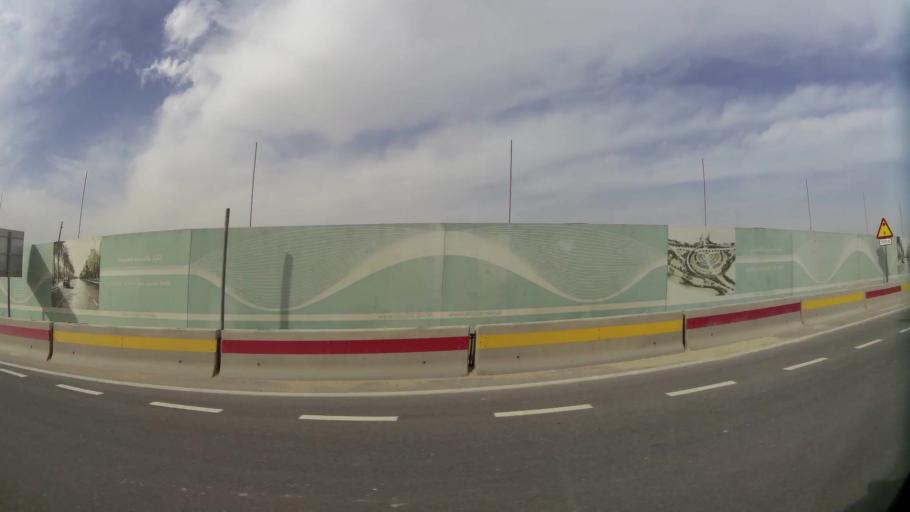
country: QA
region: Baladiyat ar Rayyan
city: Ar Rayyan
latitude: 25.3069
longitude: 51.4060
